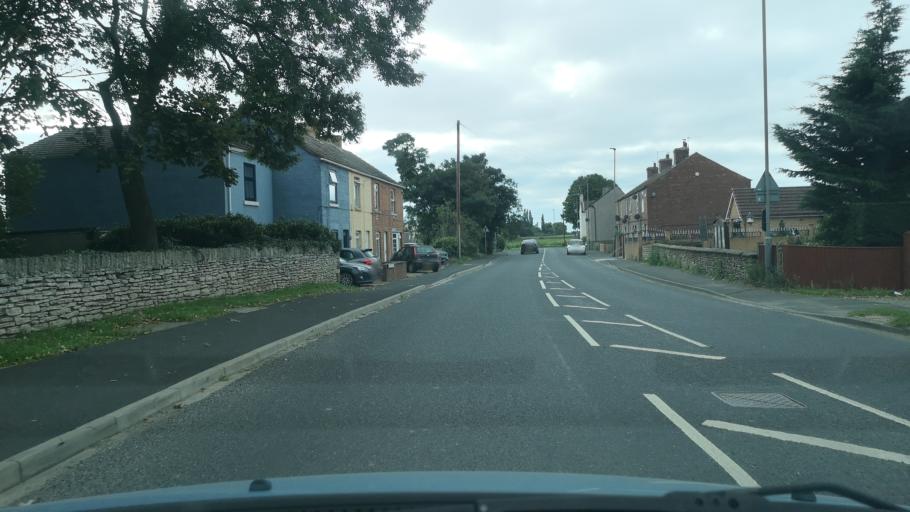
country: GB
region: England
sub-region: Doncaster
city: Norton
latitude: 53.6913
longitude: -1.1543
